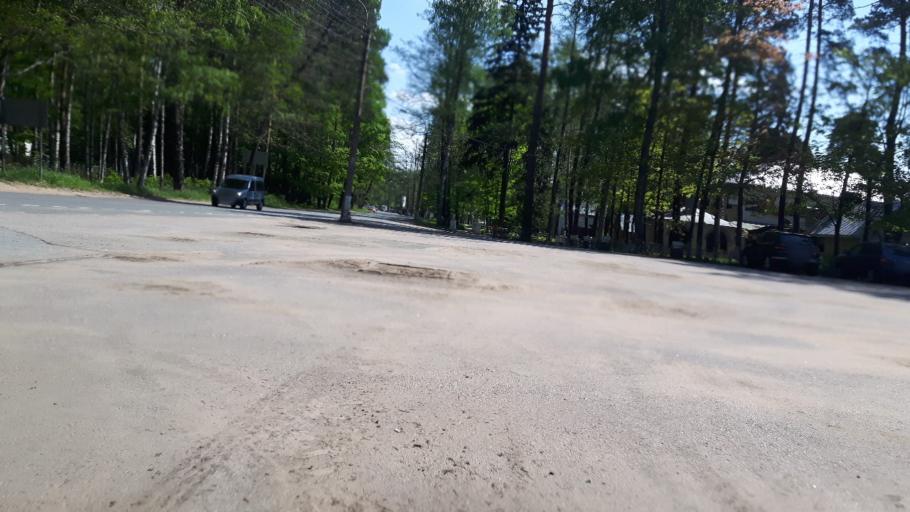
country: RU
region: St.-Petersburg
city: Komarovo
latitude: 60.1692
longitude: 29.8186
